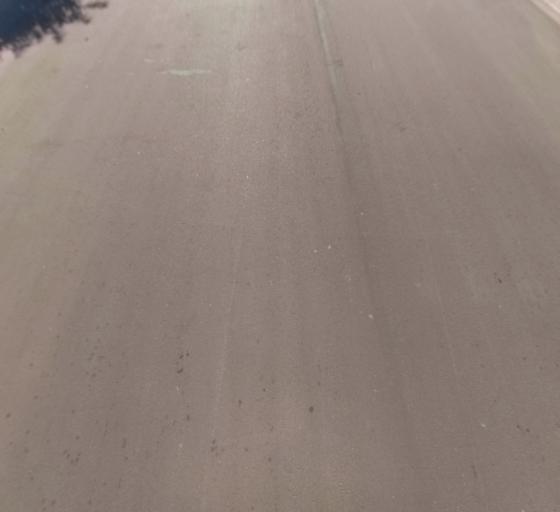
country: US
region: California
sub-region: Madera County
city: Parkwood
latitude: 36.9356
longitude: -120.0525
